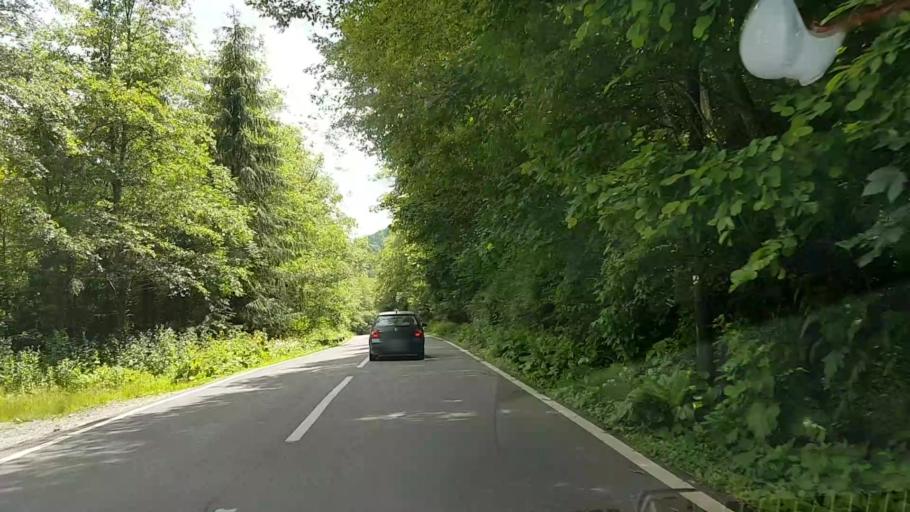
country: RO
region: Suceava
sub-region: Comuna Crucea
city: Crucea
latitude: 47.2919
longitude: 25.6319
